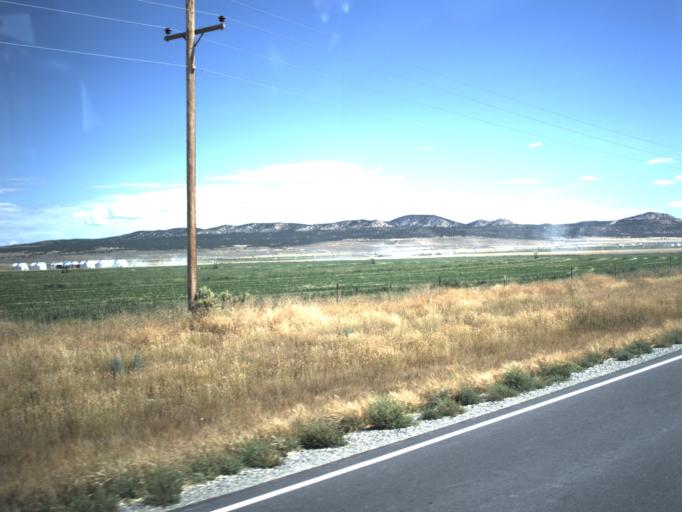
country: US
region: Idaho
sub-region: Oneida County
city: Malad City
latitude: 41.9671
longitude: -112.8592
